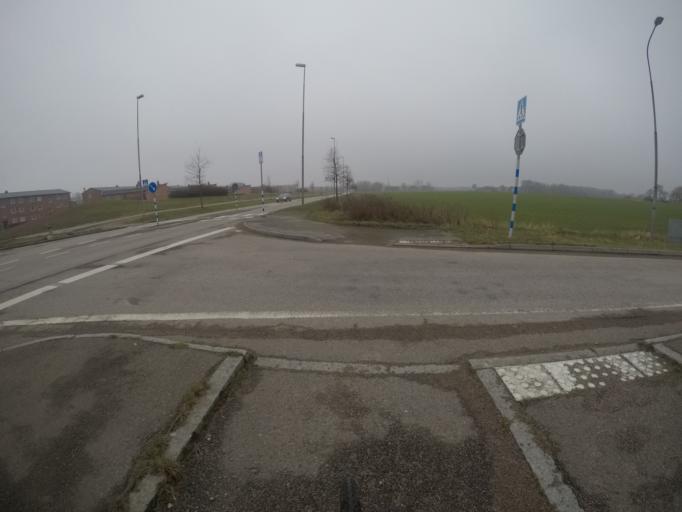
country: SE
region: Skane
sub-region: Hoganas Kommun
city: Hoganas
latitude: 56.2032
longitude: 12.5763
